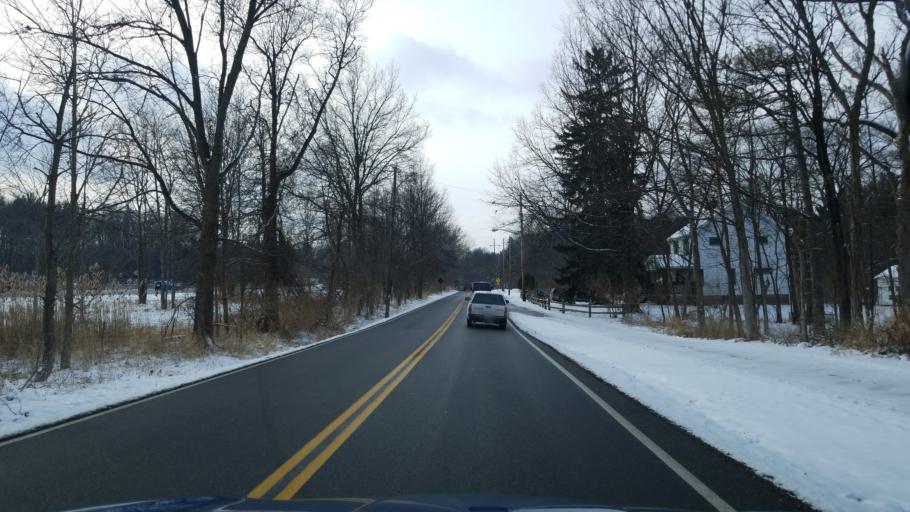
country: US
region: Ohio
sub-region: Cuyahoga County
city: Berea
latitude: 41.3428
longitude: -81.8396
